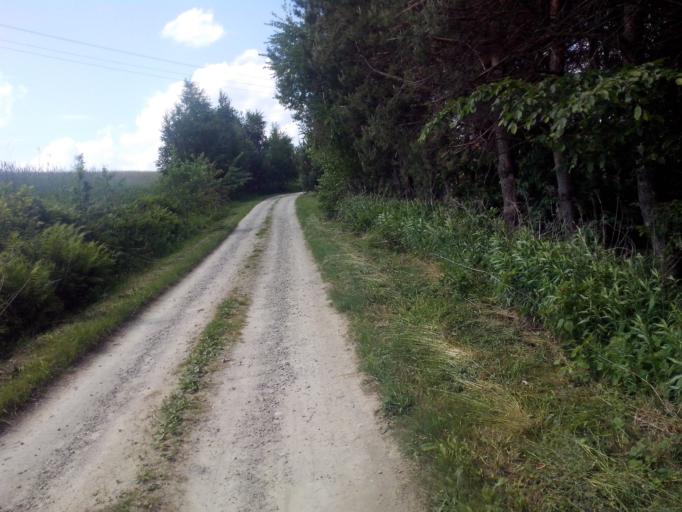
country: PL
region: Subcarpathian Voivodeship
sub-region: Powiat strzyzowski
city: Jawornik
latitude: 49.8392
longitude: 21.8558
